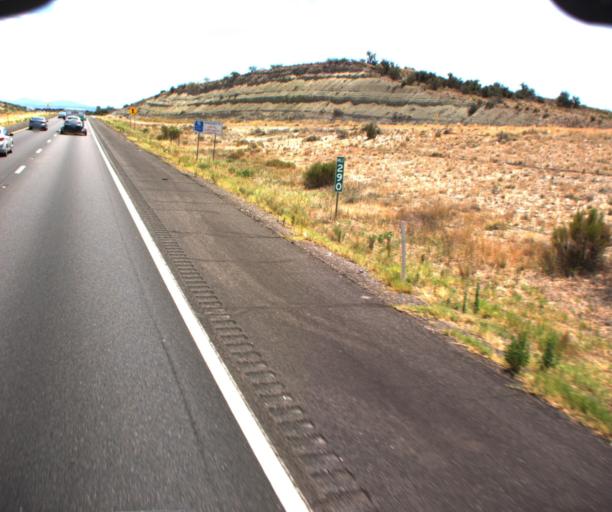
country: US
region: Arizona
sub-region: Yavapai County
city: Camp Verde
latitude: 34.6109
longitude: -111.8617
